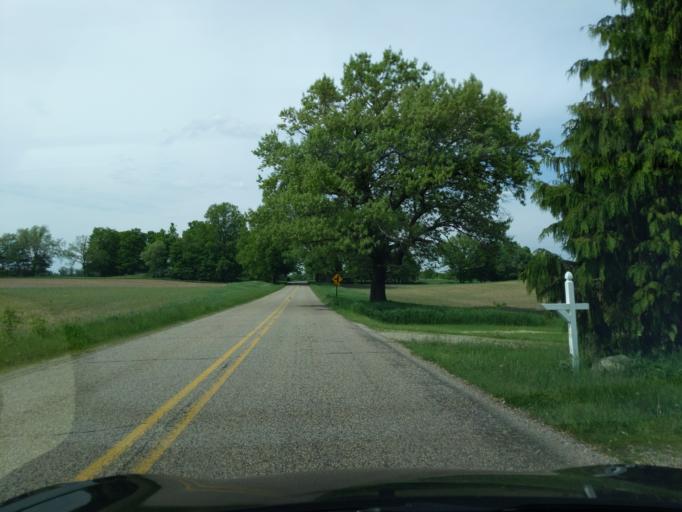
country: US
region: Michigan
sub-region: Ingham County
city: Leslie
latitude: 42.4147
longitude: -84.3334
